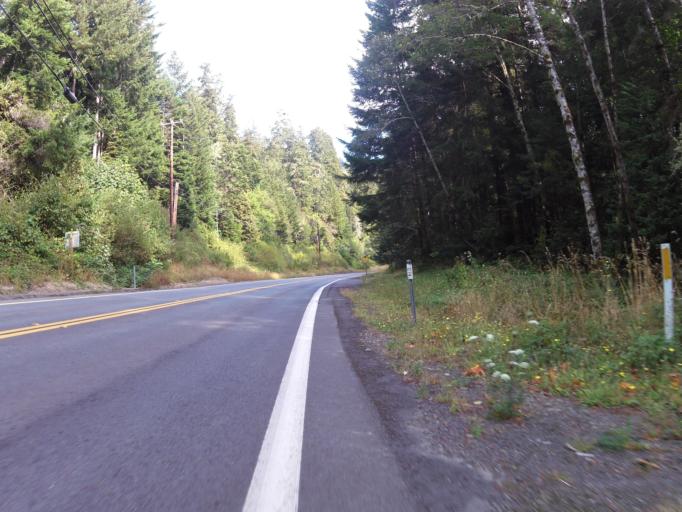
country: US
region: California
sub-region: Del Norte County
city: Bertsch-Oceanview
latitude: 41.8143
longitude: -124.0842
